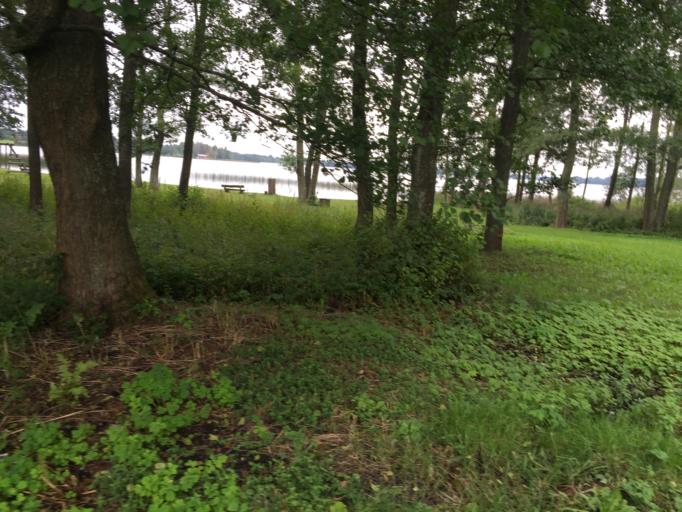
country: LV
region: Cibla
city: Cibla
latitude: 56.4091
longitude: 27.9248
